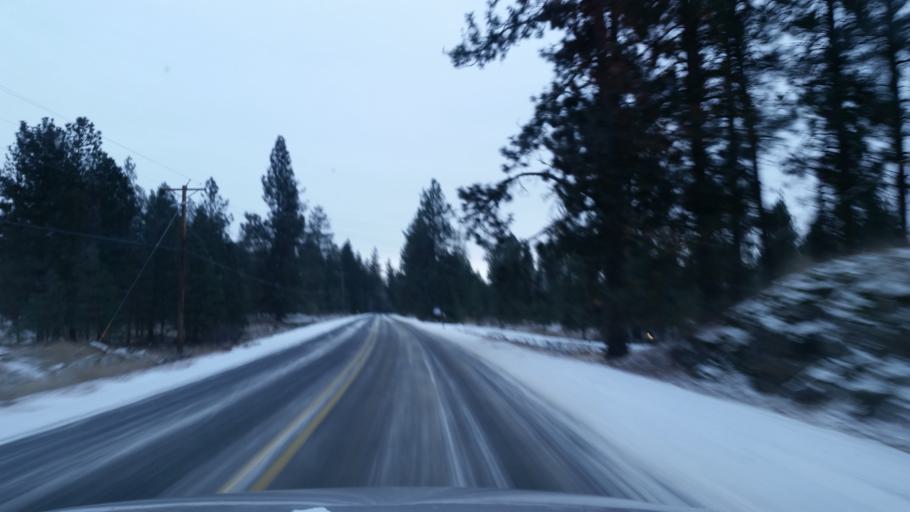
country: US
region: Washington
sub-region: Spokane County
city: Cheney
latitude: 47.4689
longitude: -117.5405
